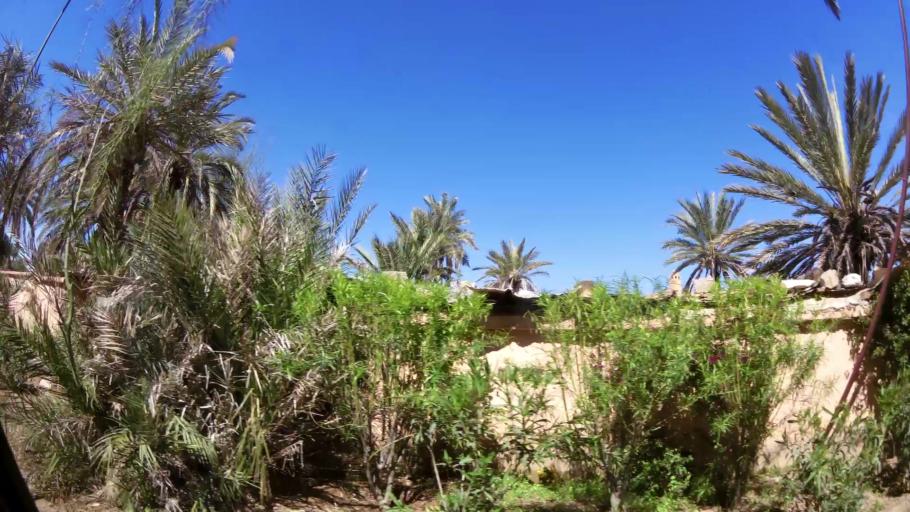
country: MA
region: Marrakech-Tensift-Al Haouz
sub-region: Marrakech
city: Marrakesh
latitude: 31.6775
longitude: -7.9732
